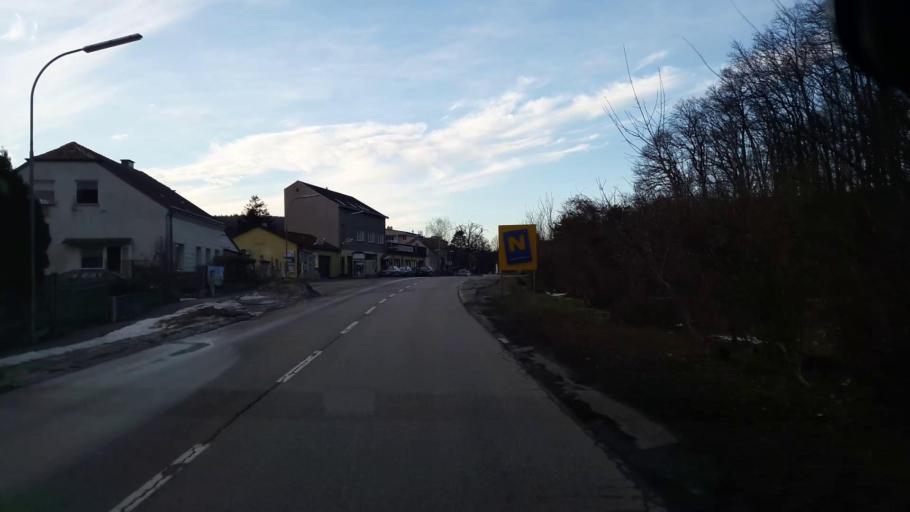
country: AT
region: Lower Austria
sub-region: Politischer Bezirk Wien-Umgebung
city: Mauerbach
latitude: 48.2328
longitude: 16.1951
